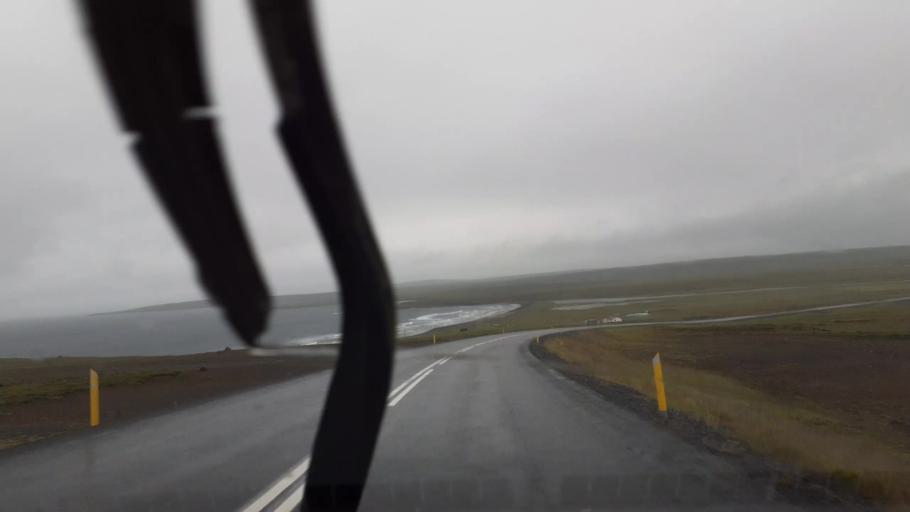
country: IS
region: Northeast
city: Husavik
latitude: 66.2299
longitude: -15.7181
